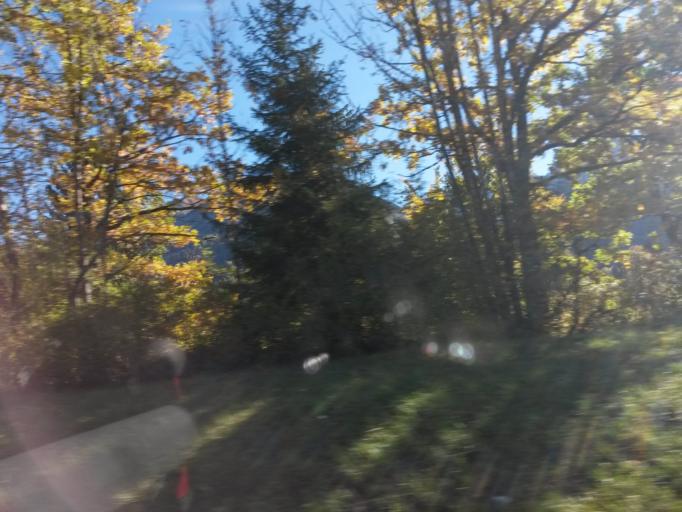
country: CH
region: Vaud
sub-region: Riviera-Pays-d'Enhaut District
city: Chateau-d'Oex
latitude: 46.5027
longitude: 7.0508
